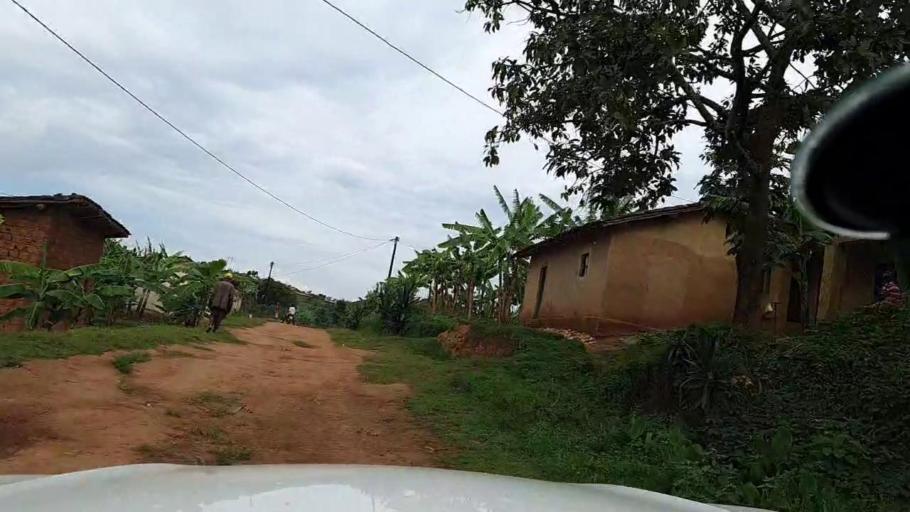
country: RW
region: Southern Province
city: Gitarama
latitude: -2.1160
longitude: 29.6412
